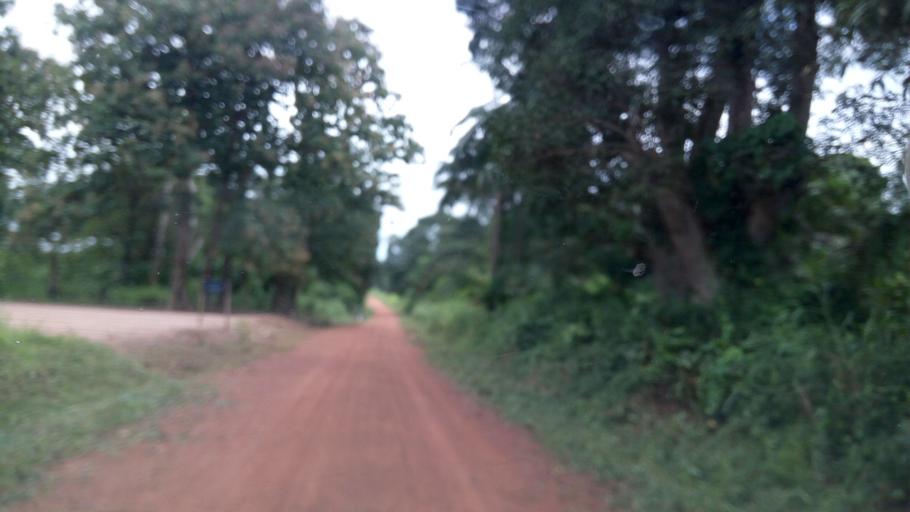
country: CD
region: Equateur
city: Libenge
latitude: 3.7370
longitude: 18.7790
